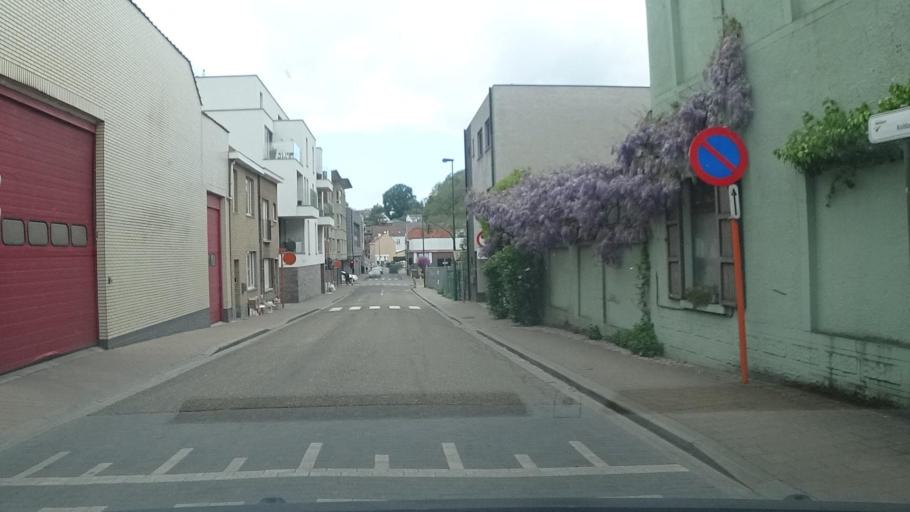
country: BE
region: Flanders
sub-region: Provincie Vlaams-Brabant
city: Hoeilaart
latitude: 50.7673
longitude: 4.4774
